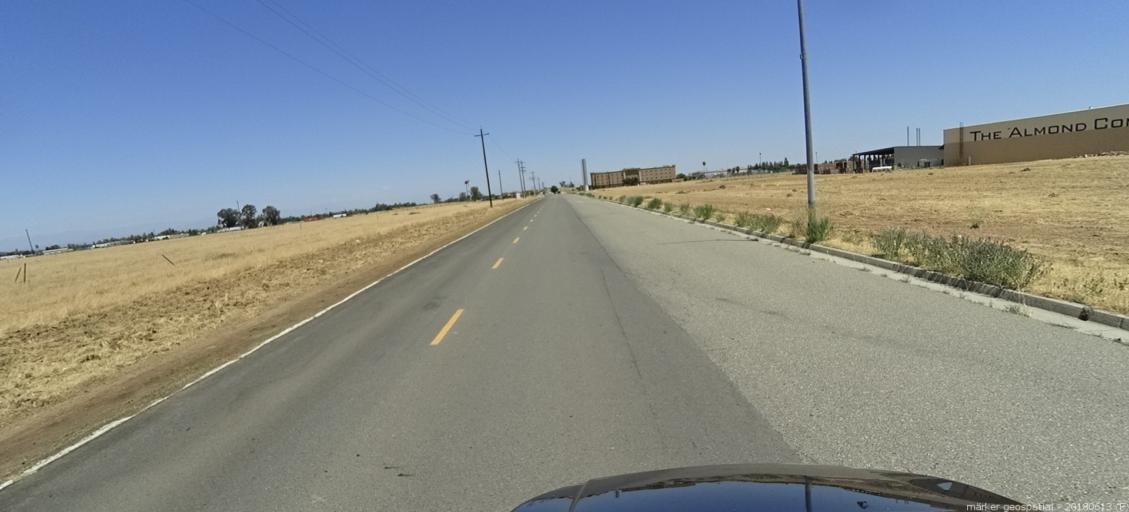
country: US
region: California
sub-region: Madera County
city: Madera Acres
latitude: 36.9965
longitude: -120.1126
